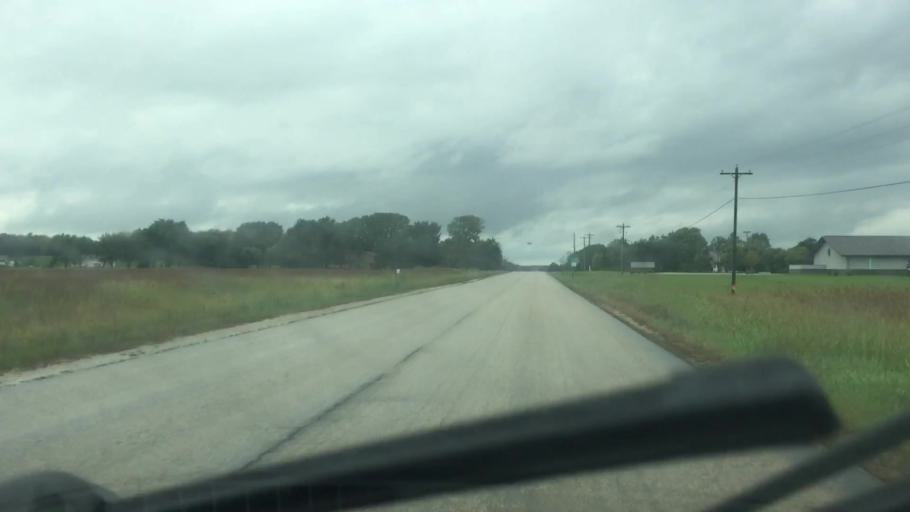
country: US
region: Kansas
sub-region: Allen County
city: Iola
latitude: 37.9513
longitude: -95.3878
